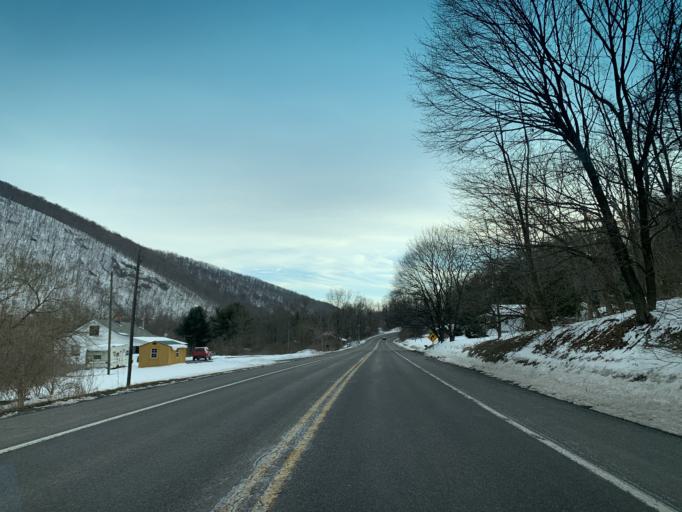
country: US
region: West Virginia
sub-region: Mineral County
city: Keyser
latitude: 39.4736
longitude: -78.9444
